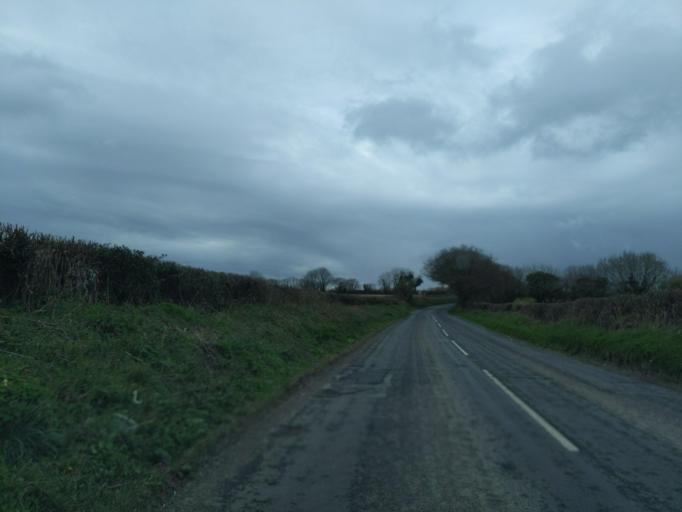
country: GB
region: England
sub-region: Cornwall
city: South Hill
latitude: 50.5467
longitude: -4.3638
